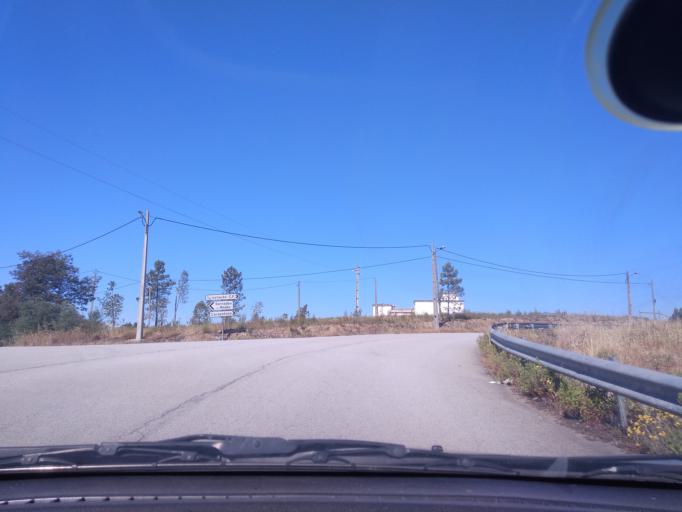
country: PT
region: Castelo Branco
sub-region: Castelo Branco
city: Castelo Branco
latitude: 39.7527
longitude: -7.6236
